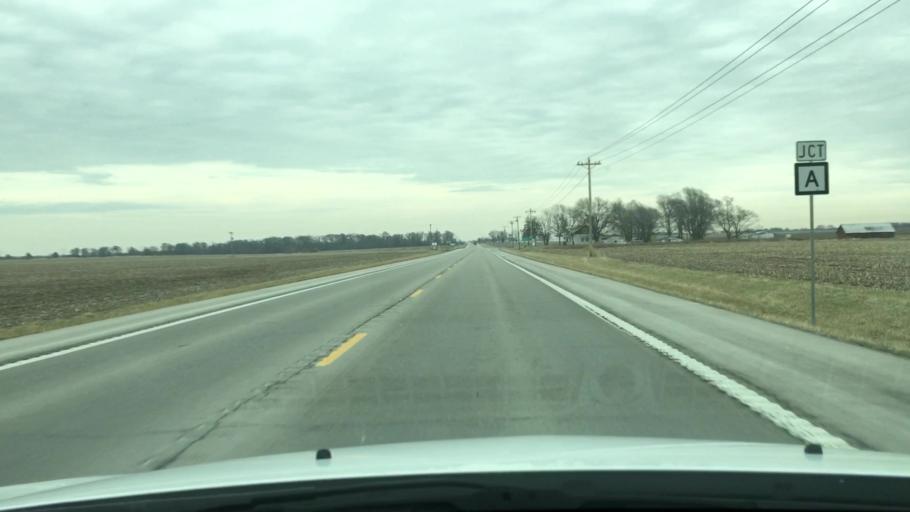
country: US
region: Missouri
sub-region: Audrain County
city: Mexico
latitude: 39.1638
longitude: -91.7655
